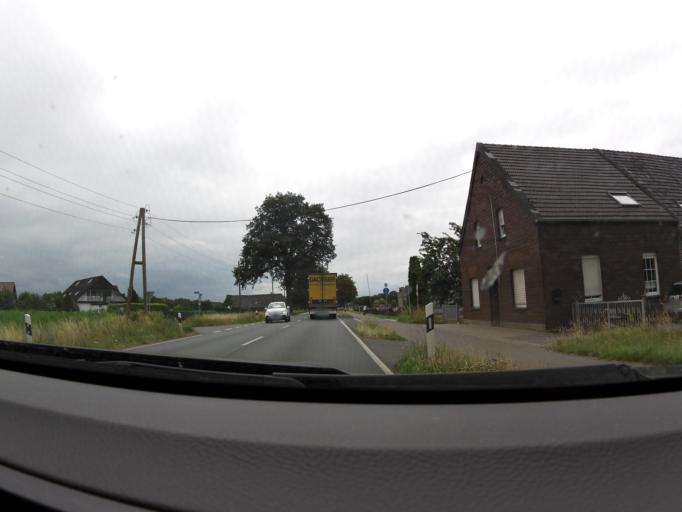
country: DE
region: North Rhine-Westphalia
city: Straelen
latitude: 51.4800
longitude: 6.2923
